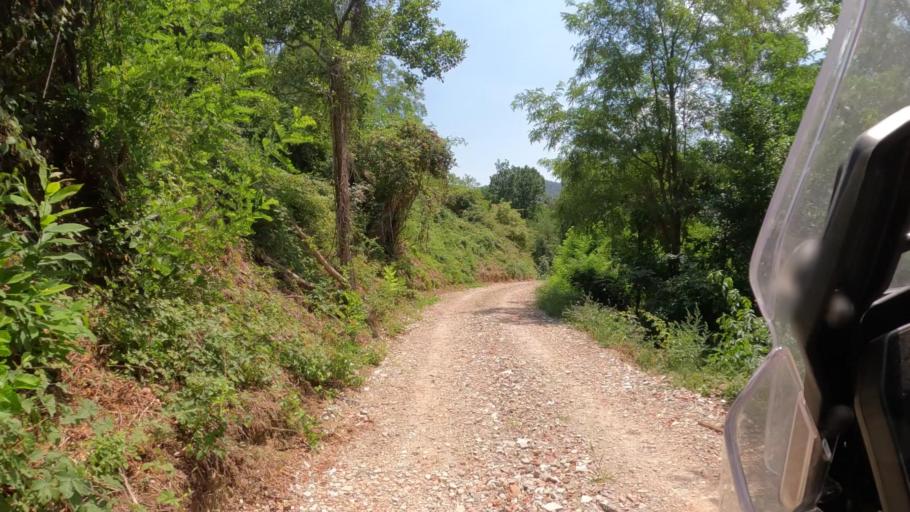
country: IT
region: Piedmont
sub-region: Provincia di Alessandria
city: Cassinelle-Concentrico
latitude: 44.5686
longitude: 8.5620
